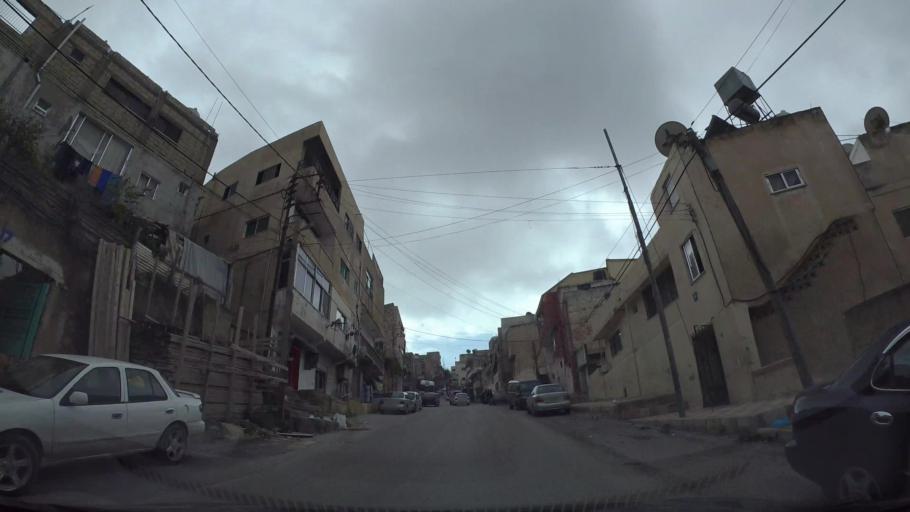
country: JO
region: Amman
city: Wadi as Sir
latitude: 31.9463
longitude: 35.8176
